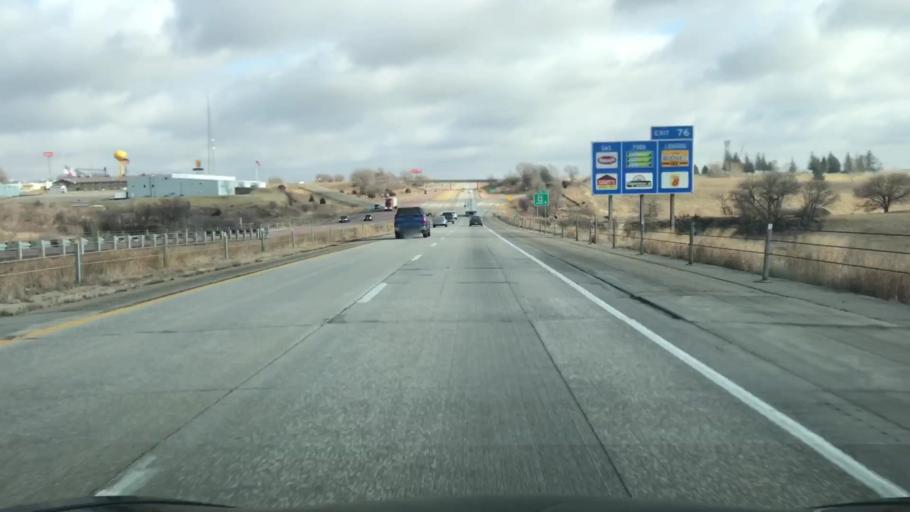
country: US
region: Iowa
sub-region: Guthrie County
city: Guthrie Center
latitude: 41.4930
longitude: -94.6510
